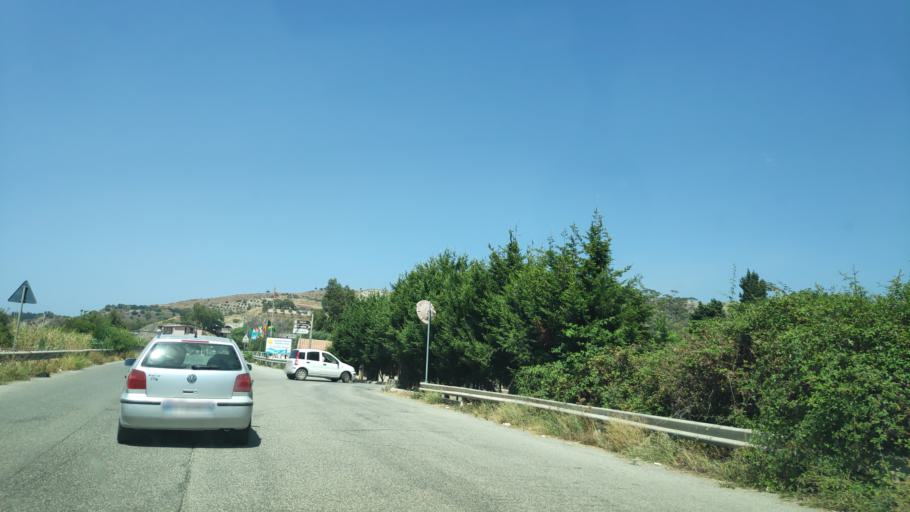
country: IT
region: Calabria
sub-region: Provincia di Reggio Calabria
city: Palizzi Marina
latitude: 37.9234
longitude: 15.9521
